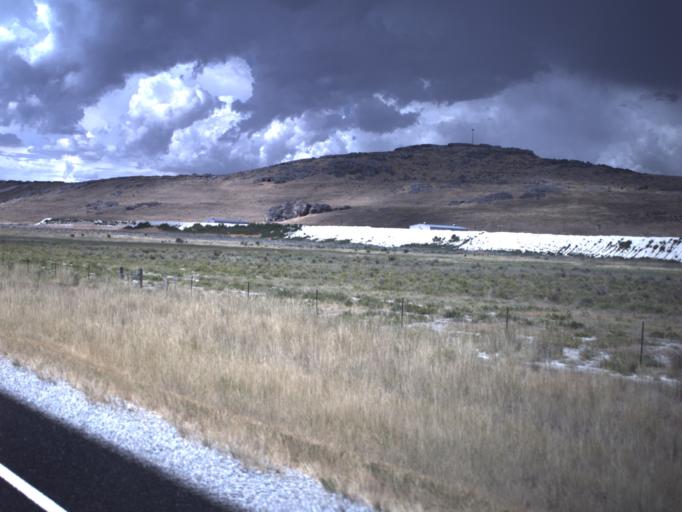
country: US
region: Utah
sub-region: Box Elder County
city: Tremonton
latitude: 41.6271
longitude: -112.3999
